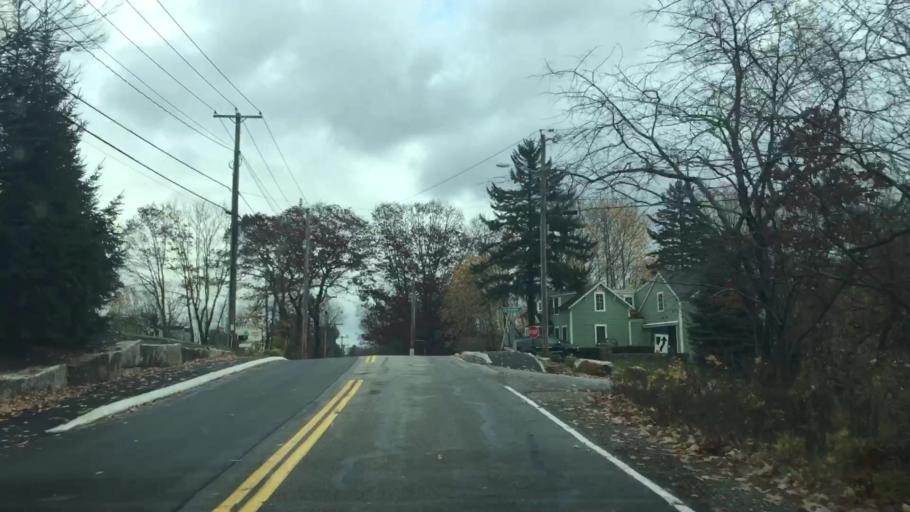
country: US
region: Maine
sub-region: York County
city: Kennebunkport
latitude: 43.3576
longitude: -70.4913
